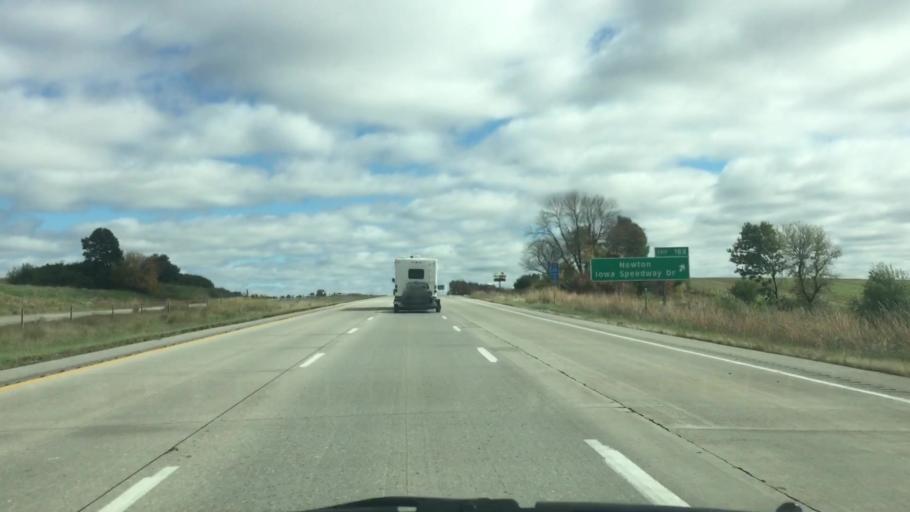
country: US
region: Iowa
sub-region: Jasper County
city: Newton
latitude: 41.6827
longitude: -93.0087
